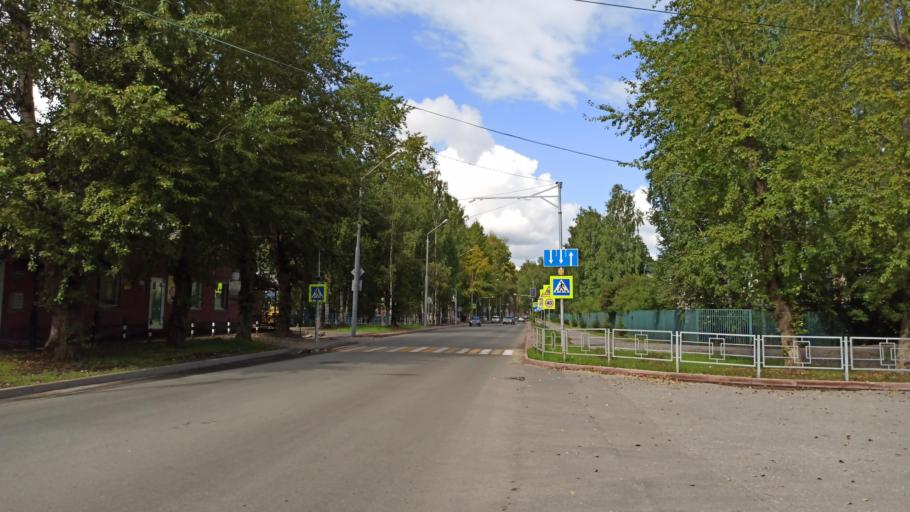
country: RU
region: Tomsk
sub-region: Tomskiy Rayon
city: Tomsk
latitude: 56.4605
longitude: 84.9816
